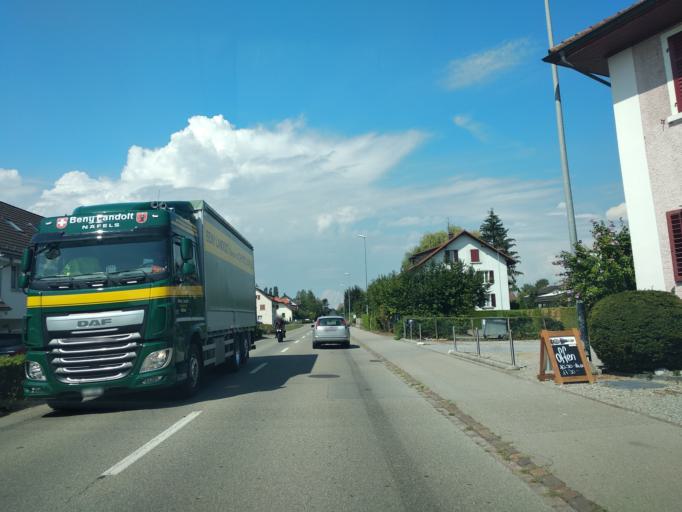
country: CH
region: Thurgau
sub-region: Frauenfeld District
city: Gachnang
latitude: 47.5686
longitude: 8.8478
